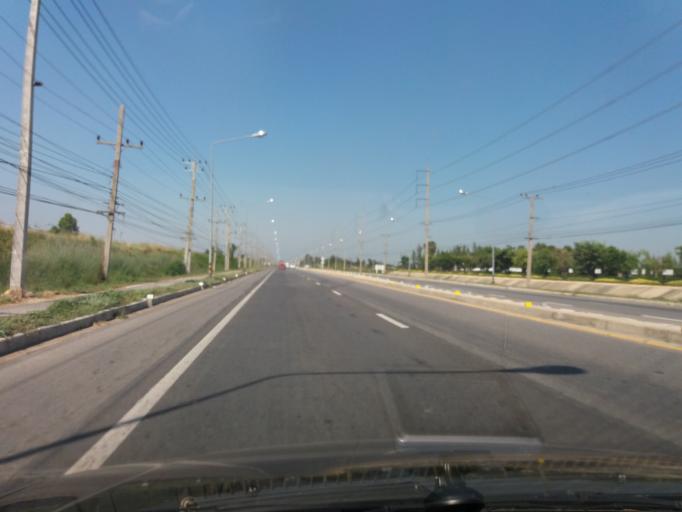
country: TH
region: Chai Nat
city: Manorom
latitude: 15.2794
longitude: 100.0957
